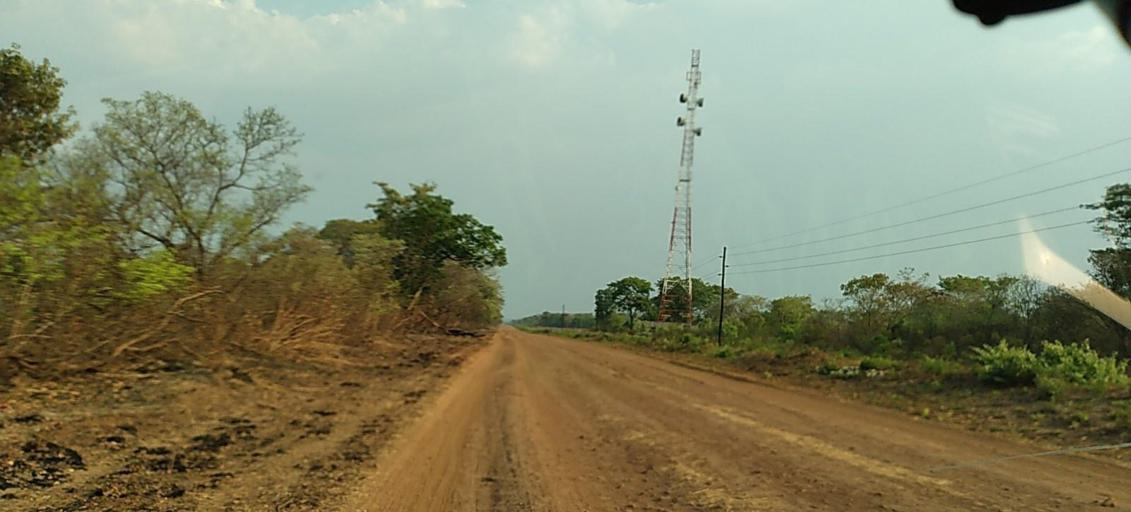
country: ZM
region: Western
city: Lukulu
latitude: -13.9965
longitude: 23.6158
